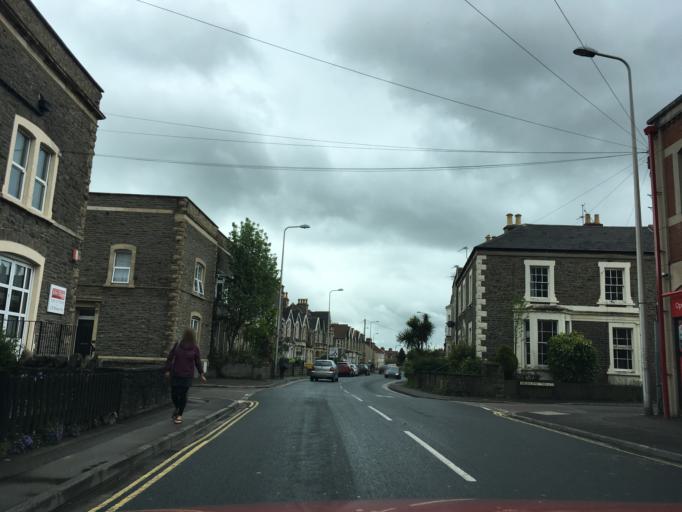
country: GB
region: England
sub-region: North Somerset
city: Clevedon
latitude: 51.4353
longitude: -2.8518
